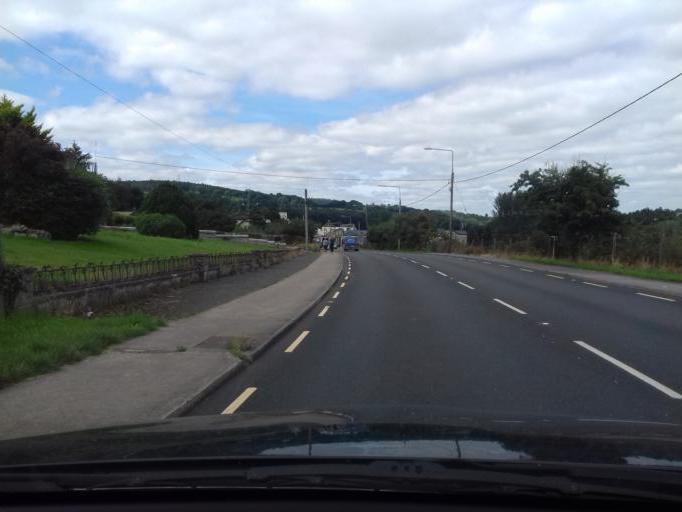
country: IE
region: Leinster
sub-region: Wicklow
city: Baltinglass
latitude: 52.9373
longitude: -6.7085
